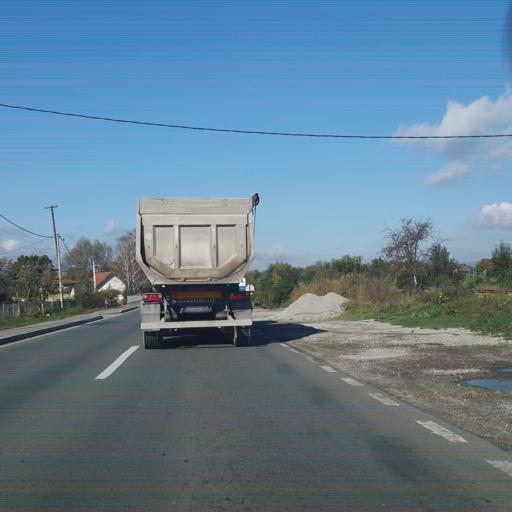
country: RS
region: Central Serbia
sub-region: Raski Okrug
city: Vrnjacka Banja
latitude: 43.6366
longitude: 20.9331
